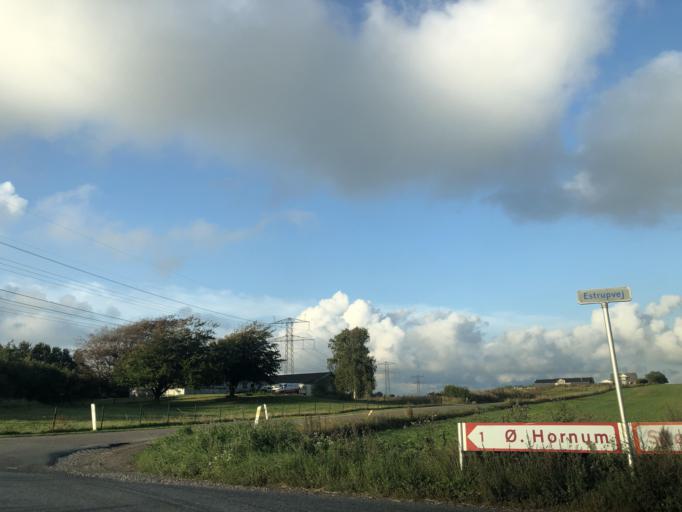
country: DK
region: North Denmark
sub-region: Rebild Kommune
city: Stovring
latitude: 56.9286
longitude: 9.7646
